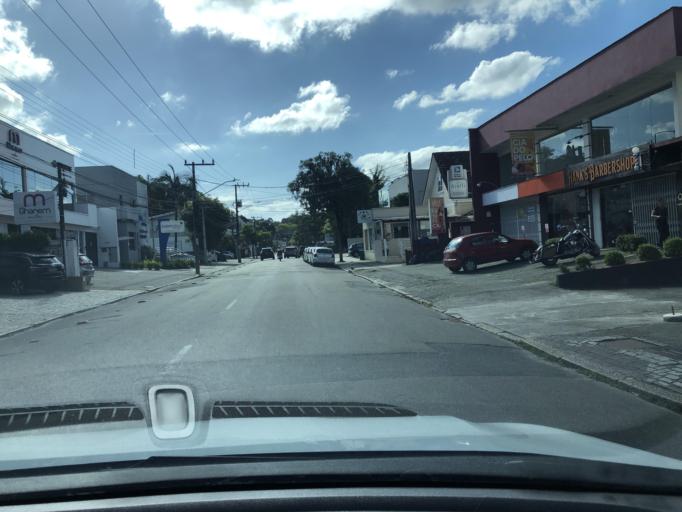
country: BR
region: Santa Catarina
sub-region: Joinville
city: Joinville
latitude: -26.2967
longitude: -48.8509
